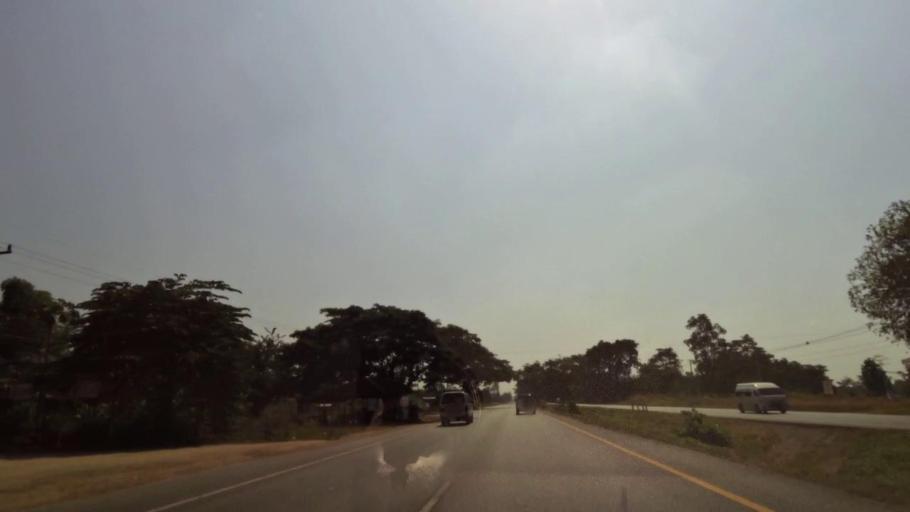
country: TH
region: Phichit
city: Bueng Na Rang
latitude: 16.3379
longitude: 100.1284
